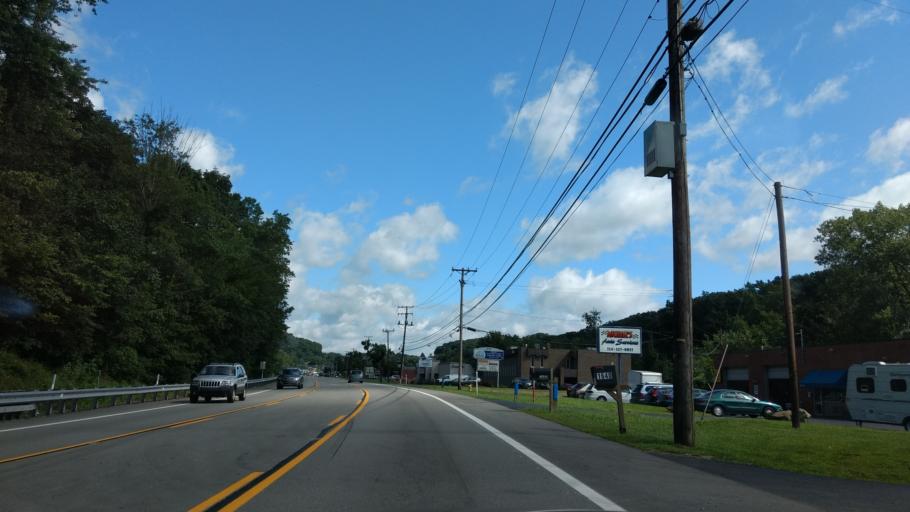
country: US
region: Pennsylvania
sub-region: Westmoreland County
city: Murrysville
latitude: 40.4381
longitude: -79.7128
